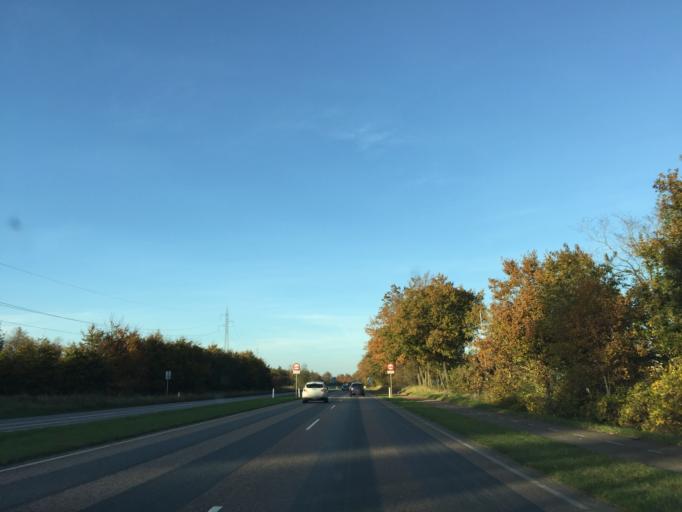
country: DK
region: South Denmark
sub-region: Aabenraa Kommune
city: Krusa
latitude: 54.8548
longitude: 9.4031
